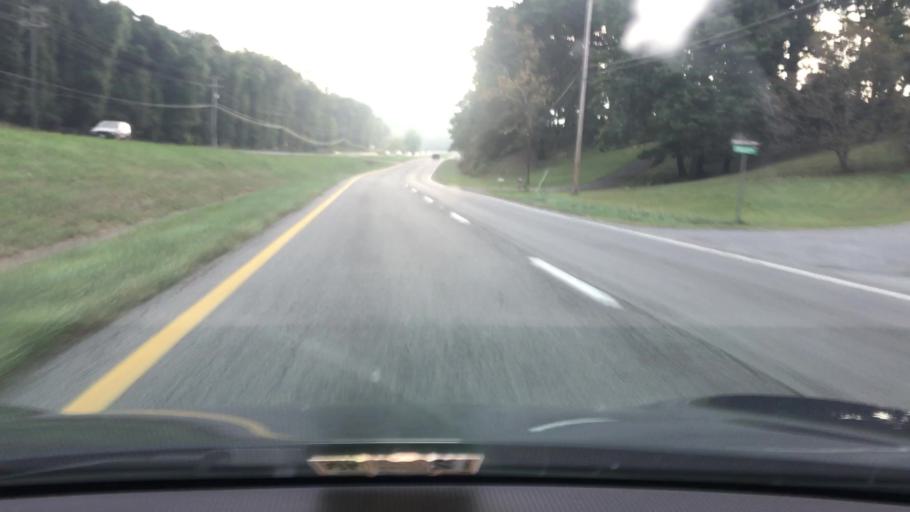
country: US
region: Virginia
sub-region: Botetourt County
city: Blue Ridge
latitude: 37.3970
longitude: -79.7629
